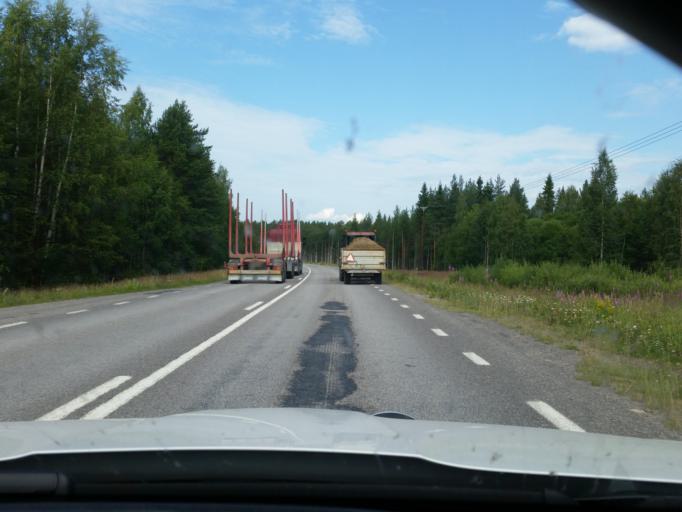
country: SE
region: Norrbotten
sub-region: Alvsbyns Kommun
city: AElvsbyn
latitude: 65.6916
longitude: 20.6846
